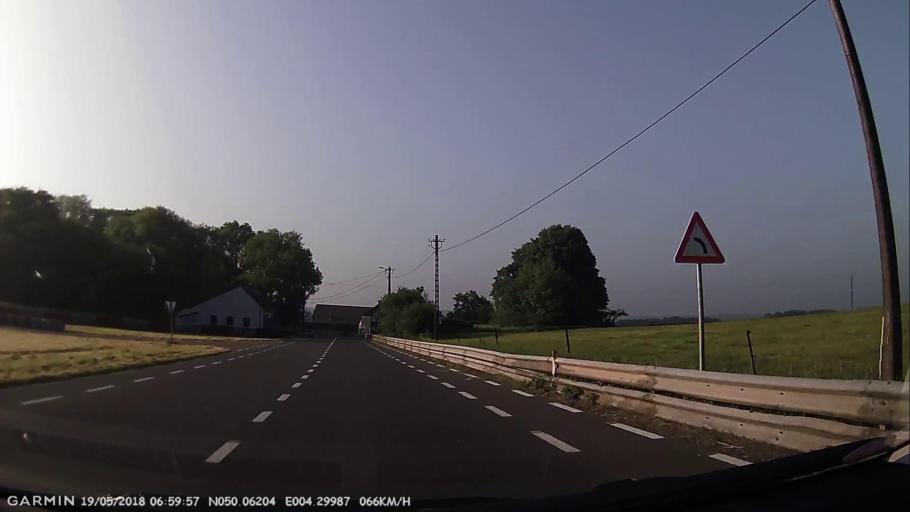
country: BE
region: Wallonia
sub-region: Province du Hainaut
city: Chimay
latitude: 50.0618
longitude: 4.3000
